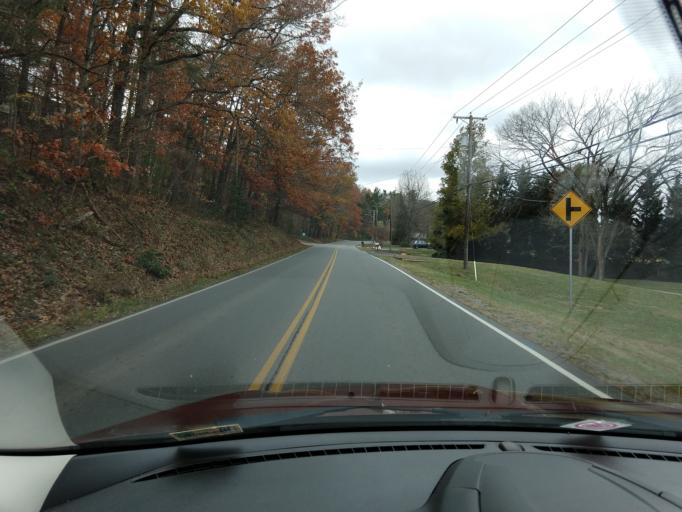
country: US
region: Virginia
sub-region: Roanoke County
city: Cave Spring
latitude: 37.2352
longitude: -79.9896
